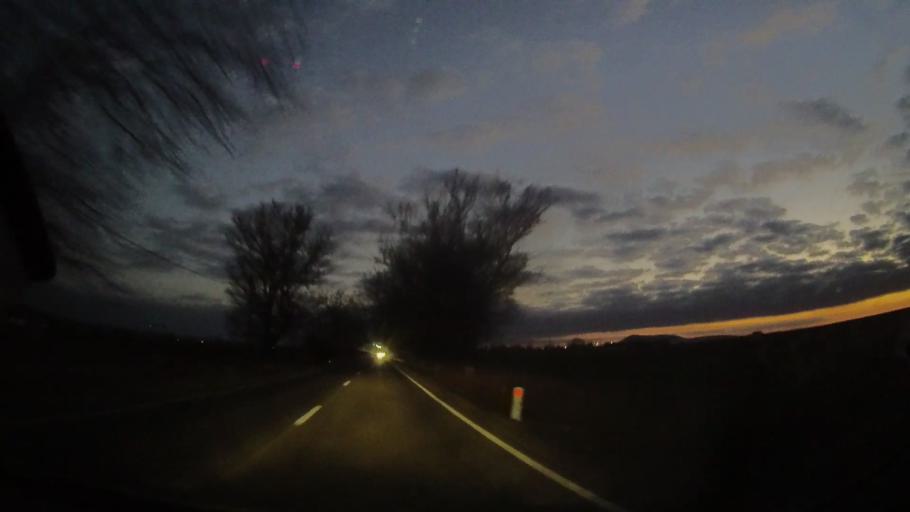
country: RO
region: Tulcea
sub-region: Comuna Mihail Kogalniceanu
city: Mihail Kogalniceanu
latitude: 45.0495
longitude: 28.7364
